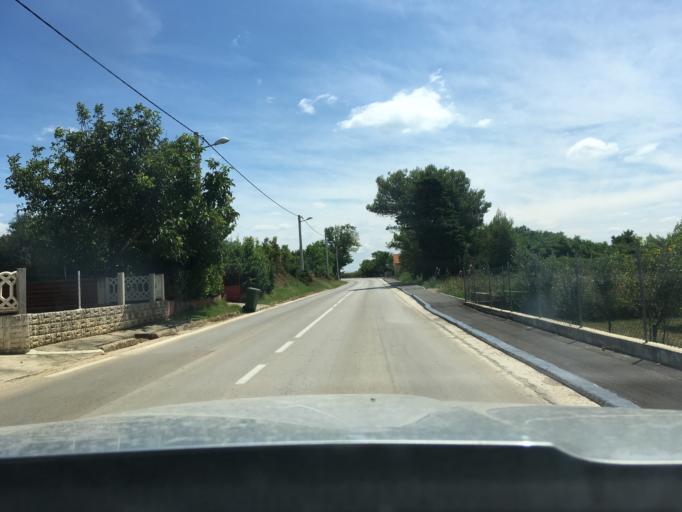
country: HR
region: Zadarska
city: Nin
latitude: 44.2471
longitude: 15.1547
